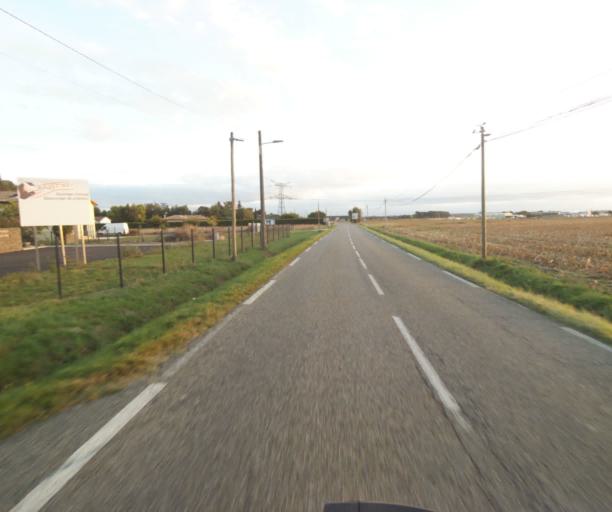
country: FR
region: Midi-Pyrenees
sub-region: Departement du Tarn-et-Garonne
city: Verdun-sur-Garonne
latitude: 43.8264
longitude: 1.2439
